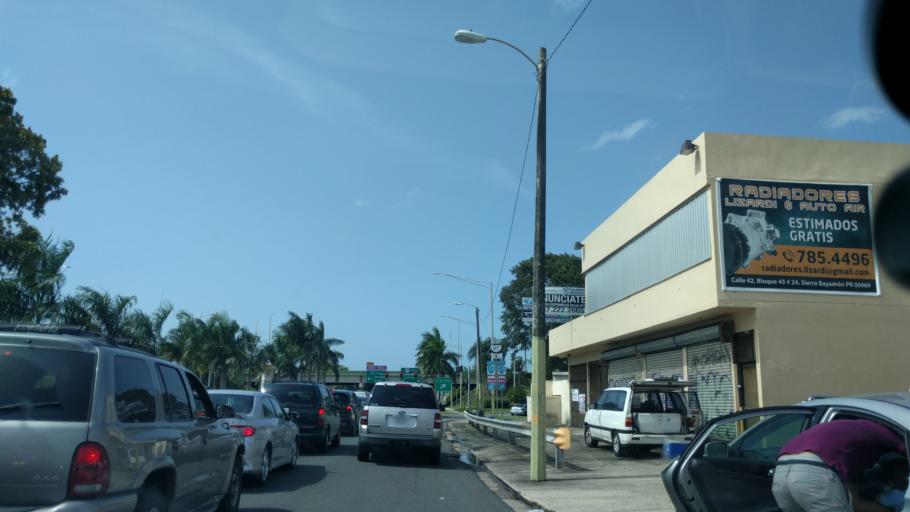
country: PR
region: Toa Baja
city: Sabana Seca
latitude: 18.4193
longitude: -66.1638
